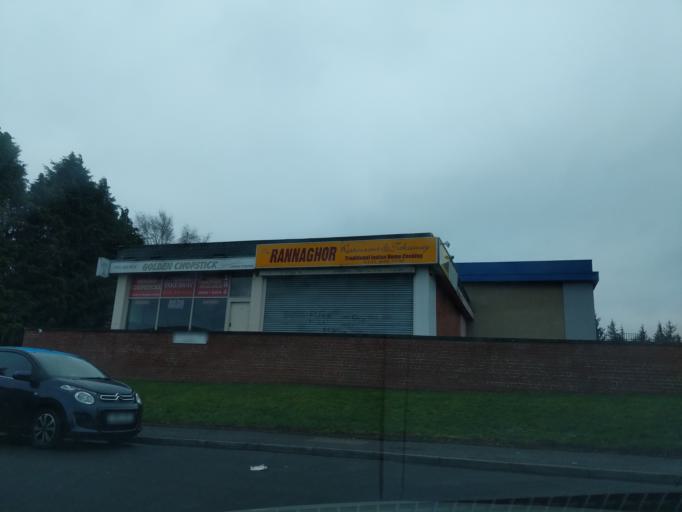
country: GB
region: Scotland
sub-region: Edinburgh
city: Currie
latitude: 55.8961
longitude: -3.3133
